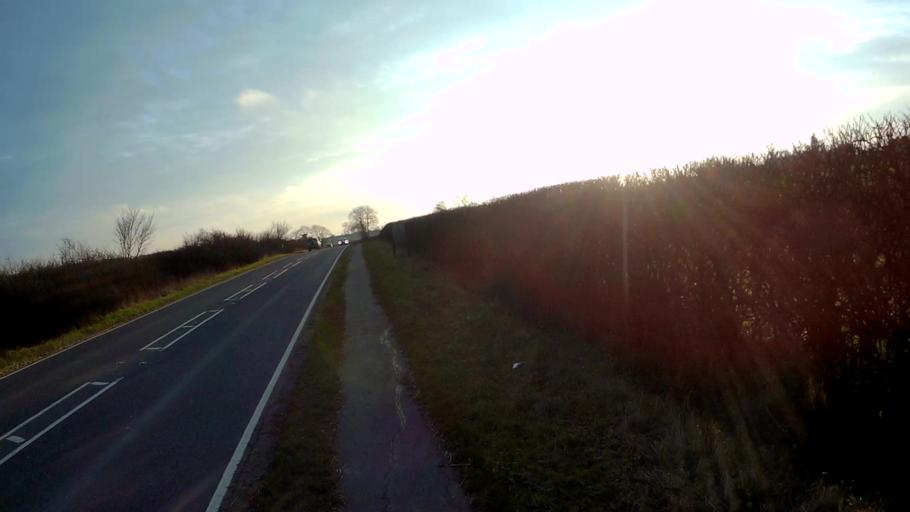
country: GB
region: England
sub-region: Lincolnshire
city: Bourne
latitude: 52.7864
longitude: -0.3777
